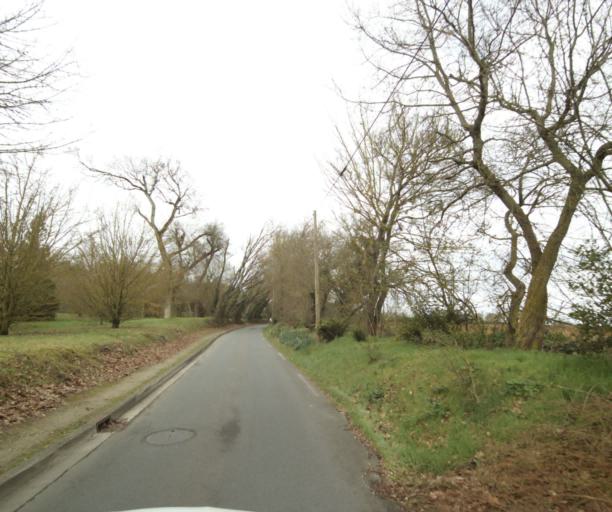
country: FR
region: Poitou-Charentes
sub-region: Departement de la Charente-Maritime
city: Lagord
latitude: 46.1889
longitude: -1.1640
